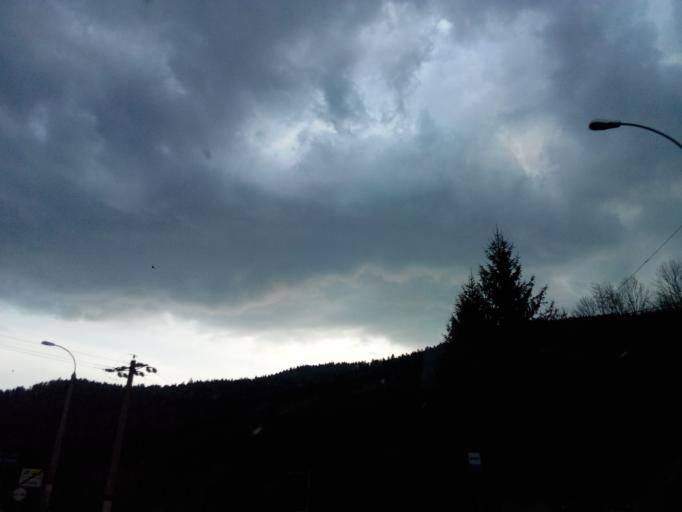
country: RO
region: Prahova
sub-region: Oras Sinaia
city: Sinaia
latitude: 45.3198
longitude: 25.5634
